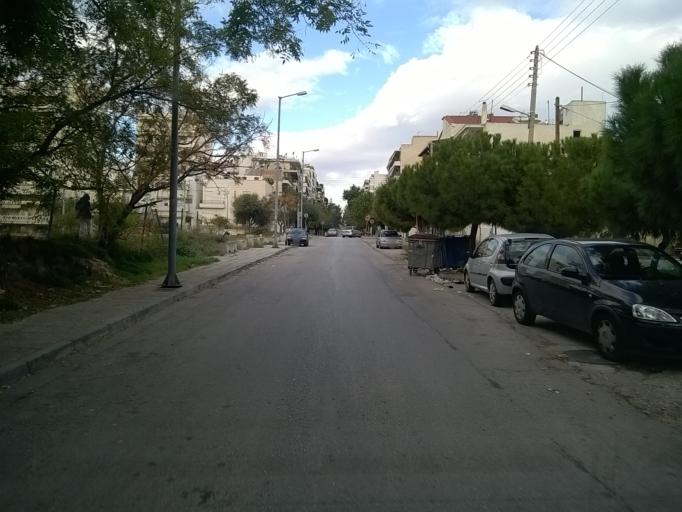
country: GR
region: Attica
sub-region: Nomarchia Athinas
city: Nea Smyrni
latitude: 37.9370
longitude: 23.7200
